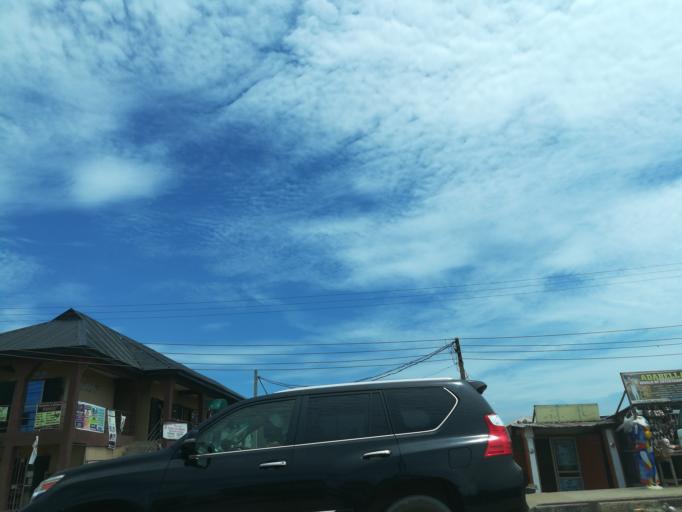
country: NG
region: Lagos
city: Ebute Ikorodu
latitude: 6.5682
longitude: 3.4797
